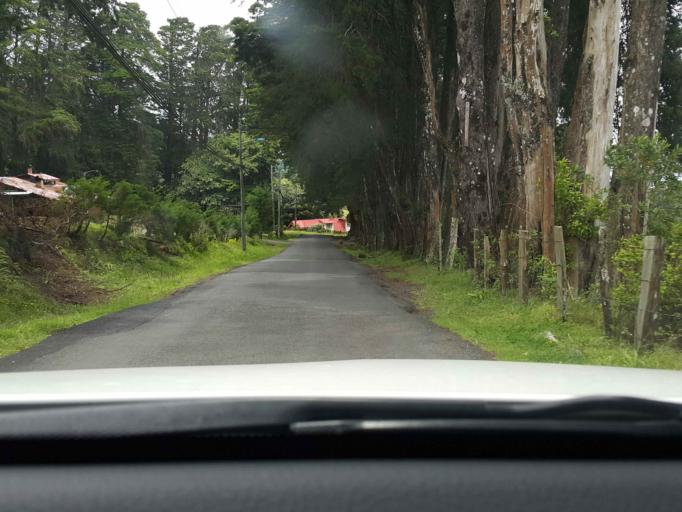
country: CR
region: Heredia
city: San Josecito
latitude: 10.0608
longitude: -84.0925
